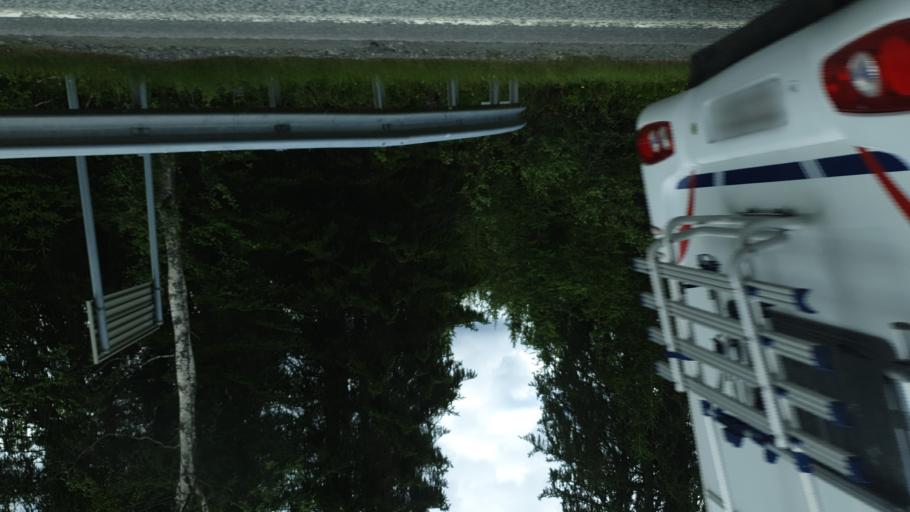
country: NO
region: Sor-Trondelag
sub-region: Rennebu
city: Berkak
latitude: 62.8879
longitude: 10.1014
